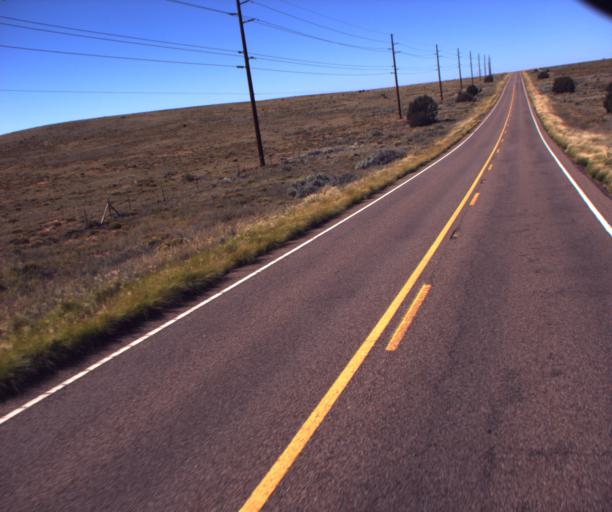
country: US
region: Arizona
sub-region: Navajo County
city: Taylor
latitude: 34.4916
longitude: -110.2234
